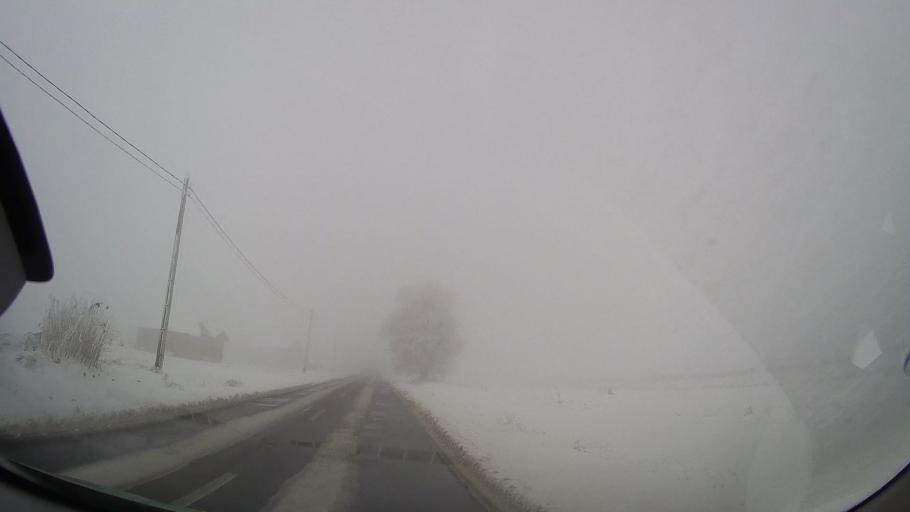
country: RO
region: Neamt
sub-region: Comuna Sabaoani
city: Sabaoani
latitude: 47.0296
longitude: 26.8586
